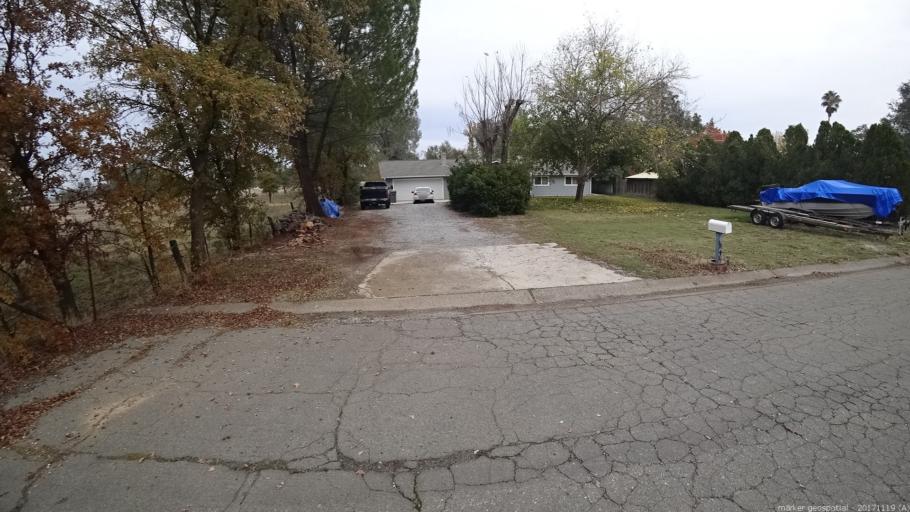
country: US
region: California
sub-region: Shasta County
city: Anderson
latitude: 40.4916
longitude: -122.3554
